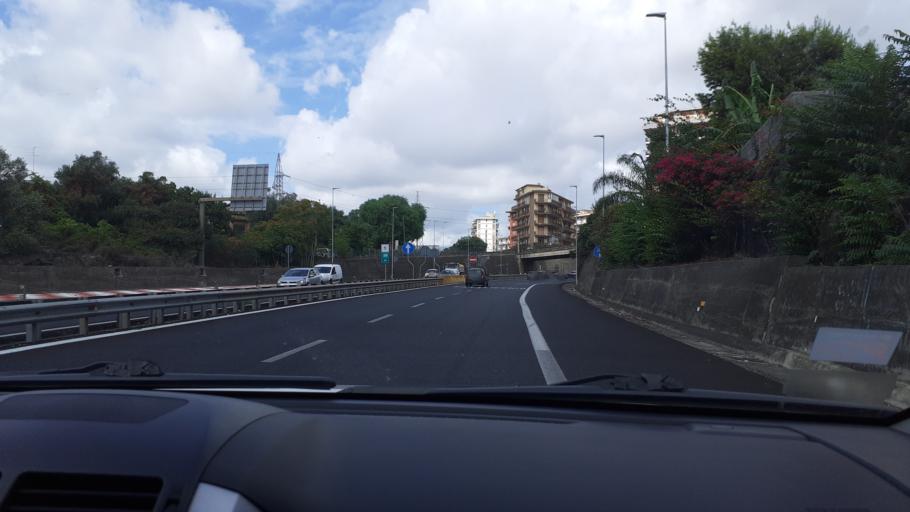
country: IT
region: Sicily
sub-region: Catania
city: Canalicchio
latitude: 37.5369
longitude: 15.0951
